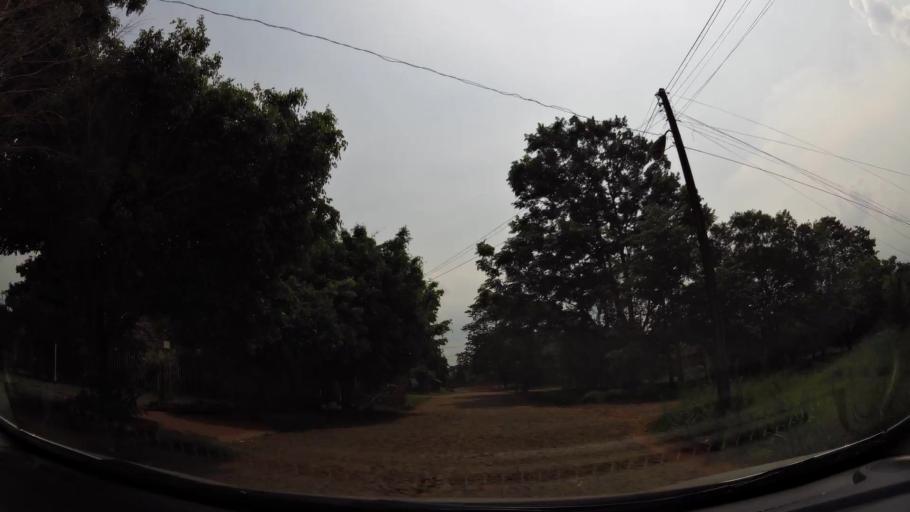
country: PY
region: Alto Parana
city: Presidente Franco
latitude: -25.5447
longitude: -54.6270
